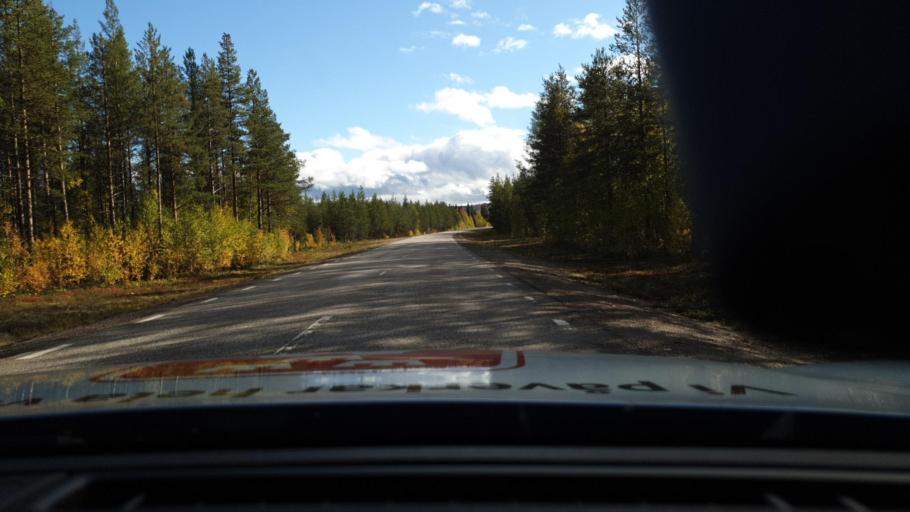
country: SE
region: Norrbotten
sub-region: Gallivare Kommun
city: Gaellivare
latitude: 67.1204
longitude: 20.9036
